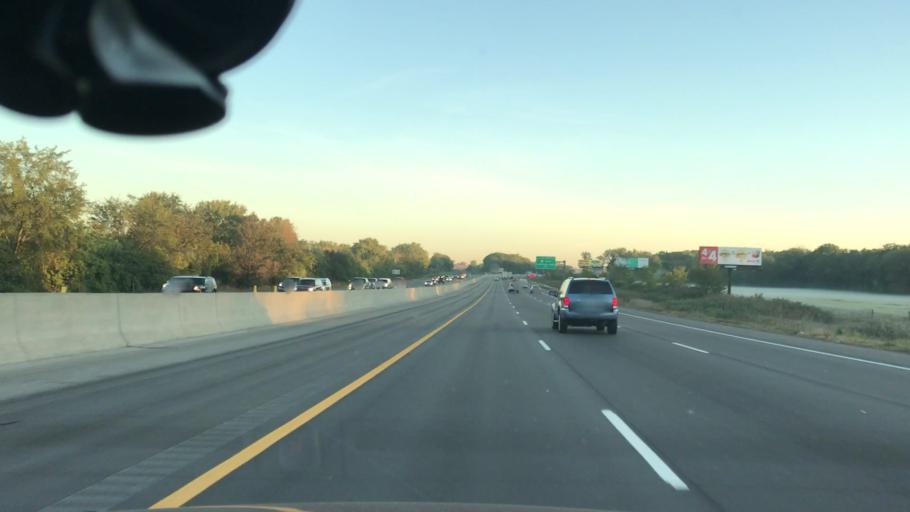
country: US
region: Michigan
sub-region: Macomb County
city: Mount Clemens
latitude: 42.6132
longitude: -82.8556
